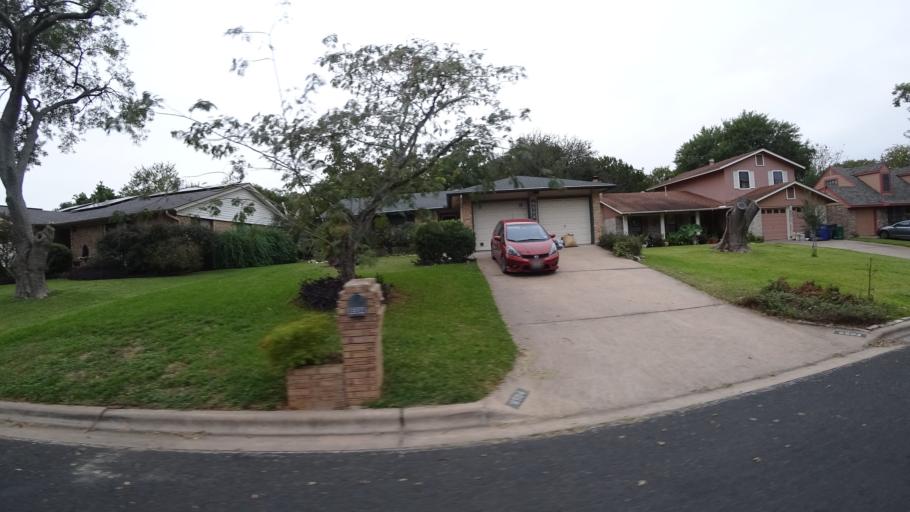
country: US
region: Texas
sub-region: Travis County
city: Onion Creek
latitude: 30.1964
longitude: -97.7817
